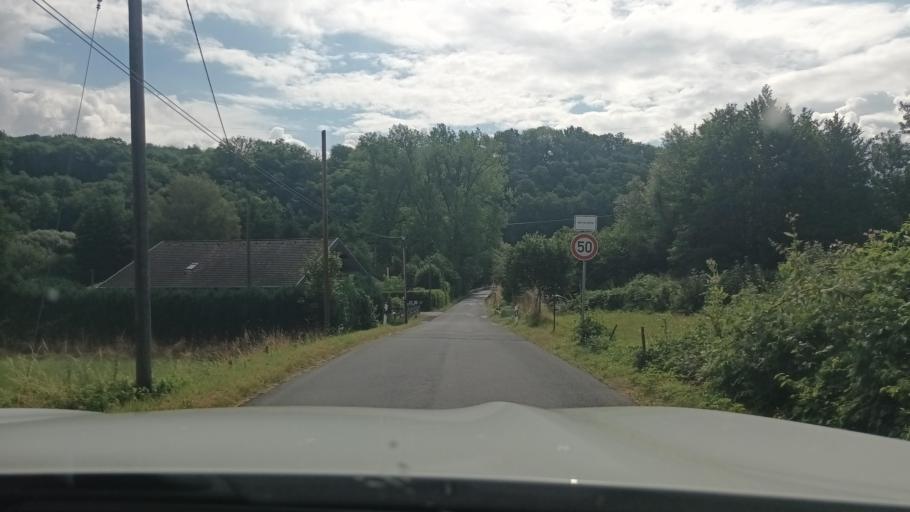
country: DE
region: North Rhine-Westphalia
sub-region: Regierungsbezirk Koln
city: Hennef
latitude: 50.7391
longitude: 7.3132
